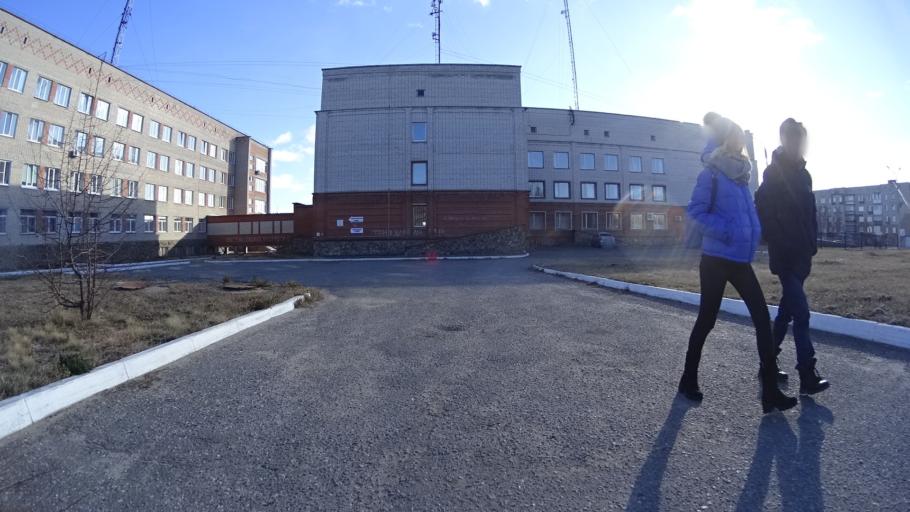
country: RU
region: Chelyabinsk
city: Troitsk
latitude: 54.0764
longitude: 61.5332
